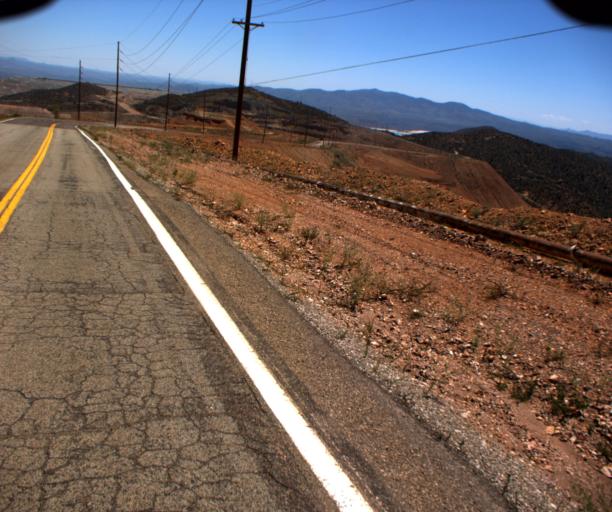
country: US
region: Arizona
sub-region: Greenlee County
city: Morenci
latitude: 33.0870
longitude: -109.3825
